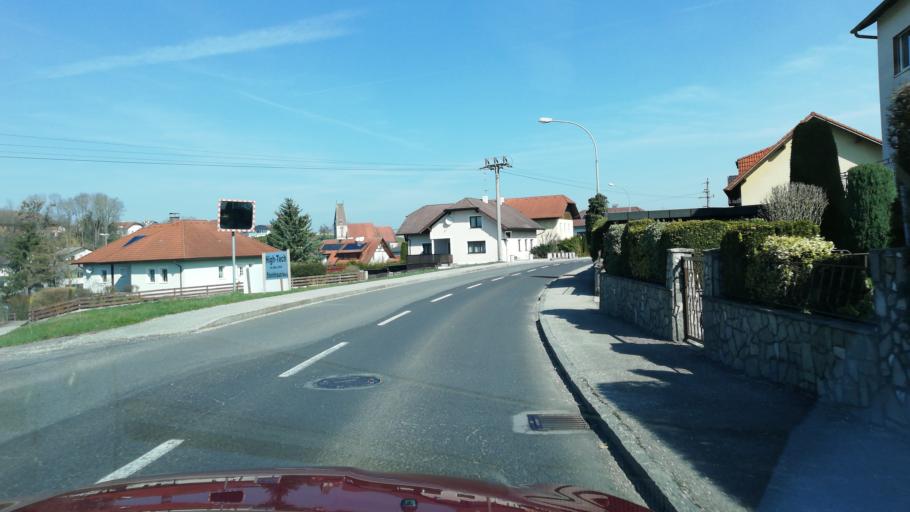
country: AT
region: Upper Austria
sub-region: Politischer Bezirk Kirchdorf an der Krems
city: Kremsmunster
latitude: 48.0943
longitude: 14.1107
